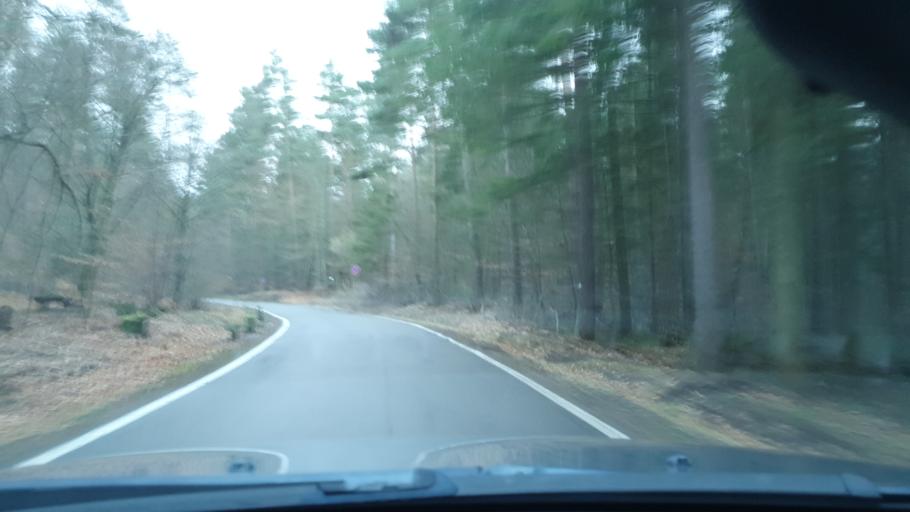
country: DE
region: Rheinland-Pfalz
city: Kaiserslautern
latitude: 49.4268
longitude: 7.7690
